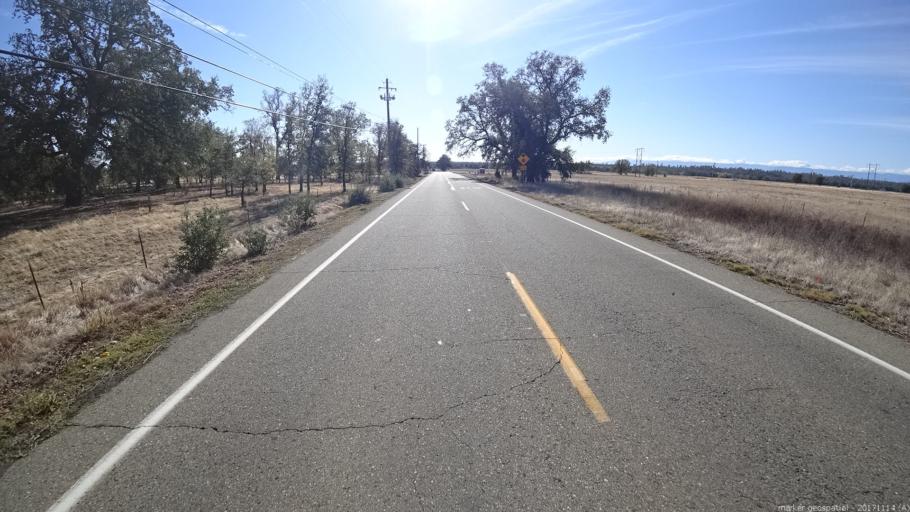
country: US
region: California
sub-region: Shasta County
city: Anderson
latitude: 40.3908
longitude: -122.4068
